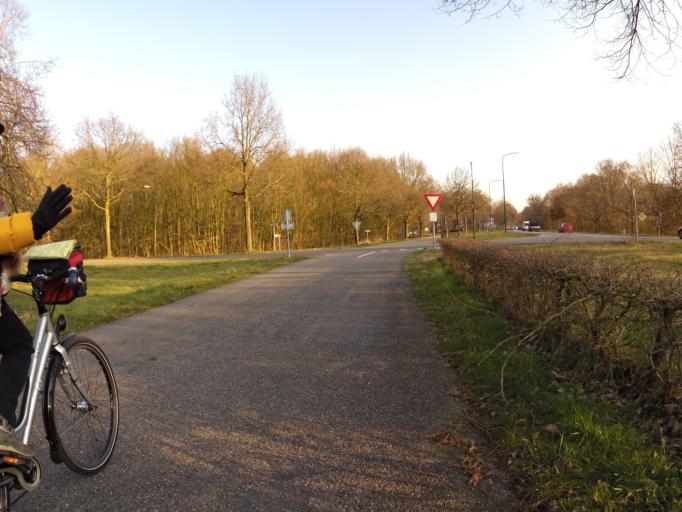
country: NL
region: North Brabant
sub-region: Gemeente Sint-Michielsgestel
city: Sint-Michielsgestel
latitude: 51.6968
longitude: 5.3687
